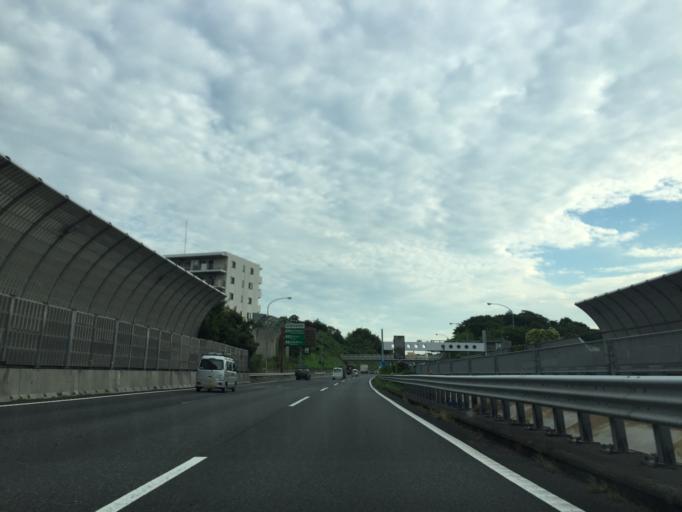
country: JP
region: Tokyo
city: Chofugaoka
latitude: 35.5680
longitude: 139.5620
